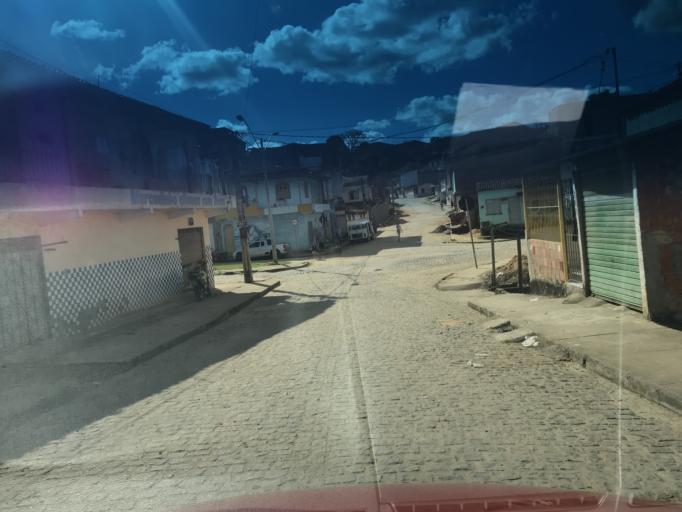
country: BR
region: Bahia
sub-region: Gandu
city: Gandu
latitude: -13.7478
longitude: -39.4916
